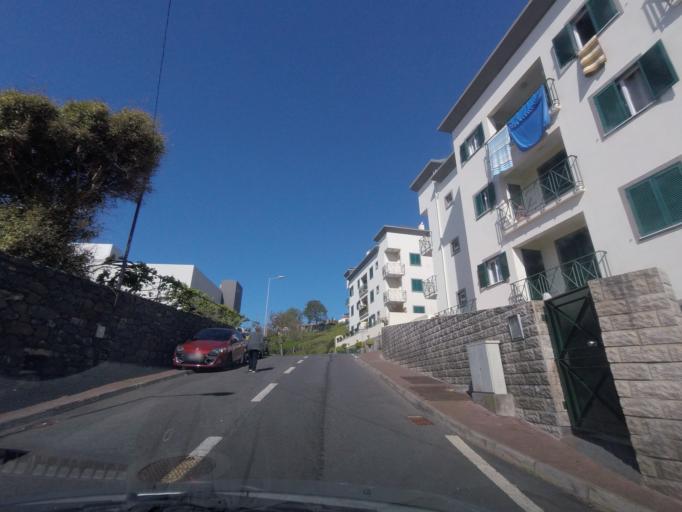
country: PT
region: Madeira
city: Camara de Lobos
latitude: 32.6703
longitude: -16.9763
